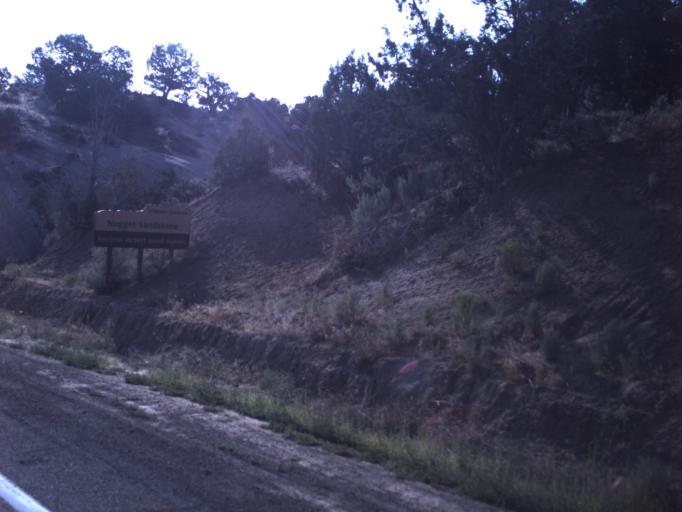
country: US
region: Utah
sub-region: Uintah County
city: Vernal
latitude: 40.5838
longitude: -109.4709
